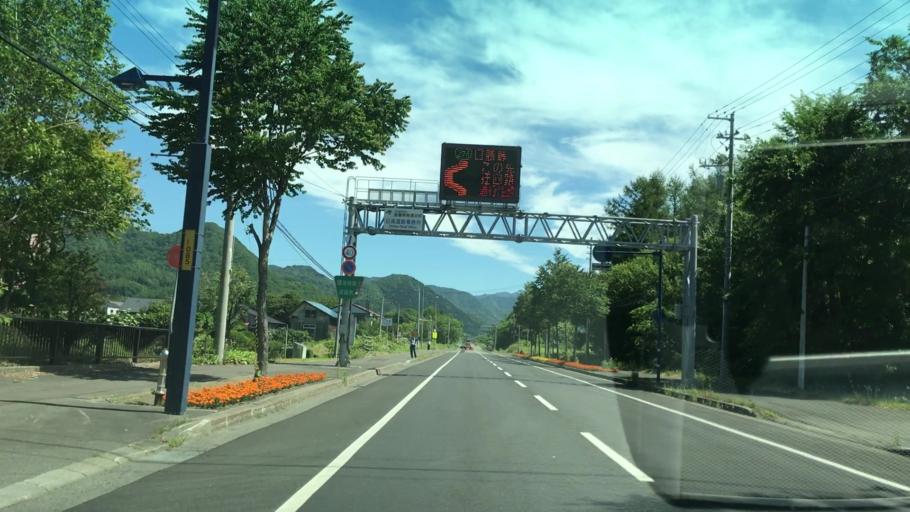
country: JP
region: Hokkaido
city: Shimo-furano
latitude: 42.8798
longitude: 142.4490
